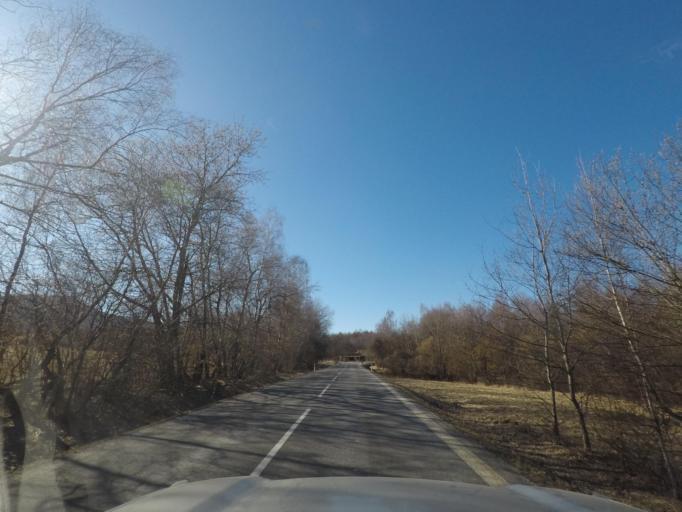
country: SK
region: Presovsky
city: Snina
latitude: 48.9359
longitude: 22.2779
